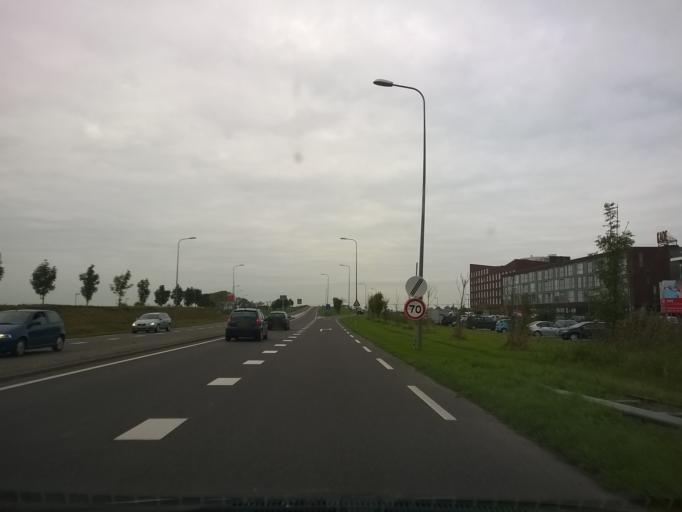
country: NL
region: Groningen
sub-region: Gemeente Groningen
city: Korrewegwijk
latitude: 53.2348
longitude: 6.5240
